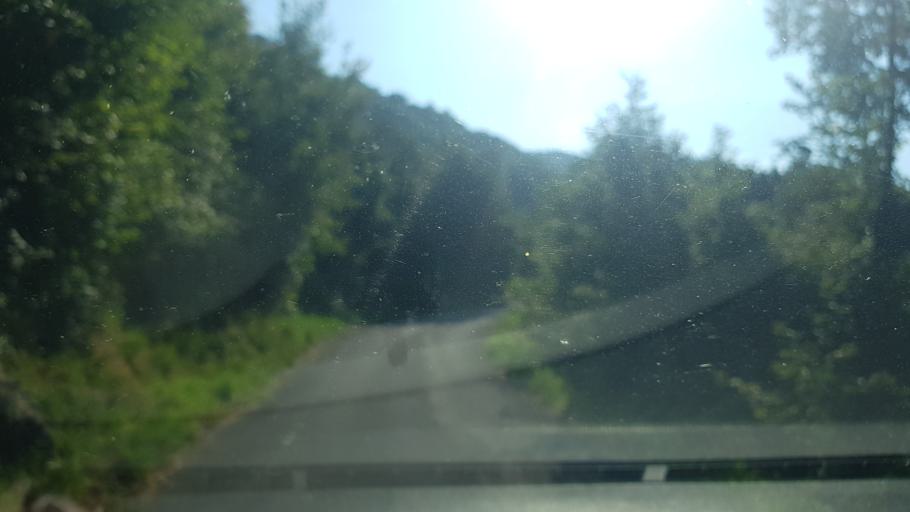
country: IT
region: Friuli Venezia Giulia
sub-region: Provincia di Udine
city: Tarcento
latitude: 46.2341
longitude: 13.2396
